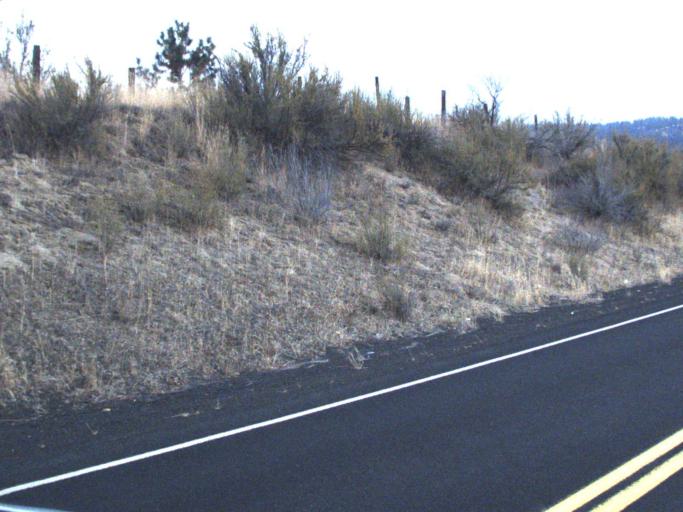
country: US
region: Washington
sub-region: Lincoln County
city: Davenport
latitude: 47.8954
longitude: -118.2735
